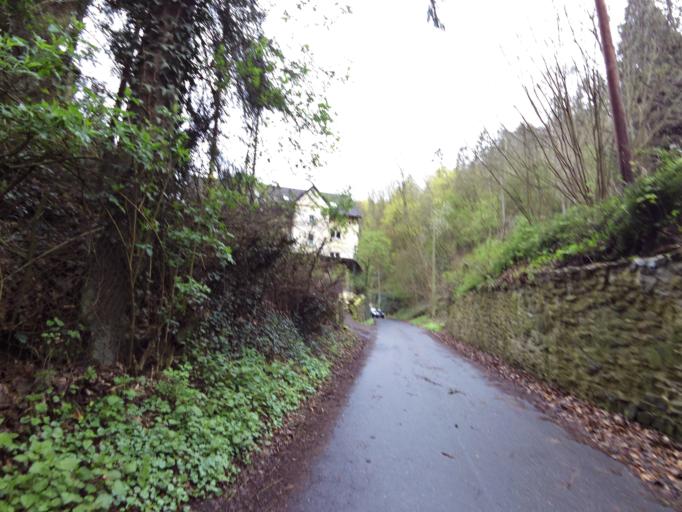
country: DE
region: Rheinland-Pfalz
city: Urbar
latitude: 50.3571
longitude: 7.6207
